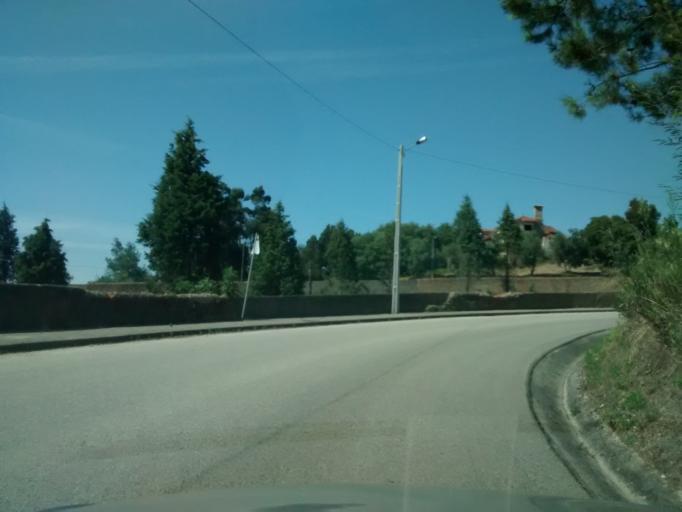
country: PT
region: Aveiro
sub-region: Mealhada
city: Mealhada
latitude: 40.3872
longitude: -8.3872
